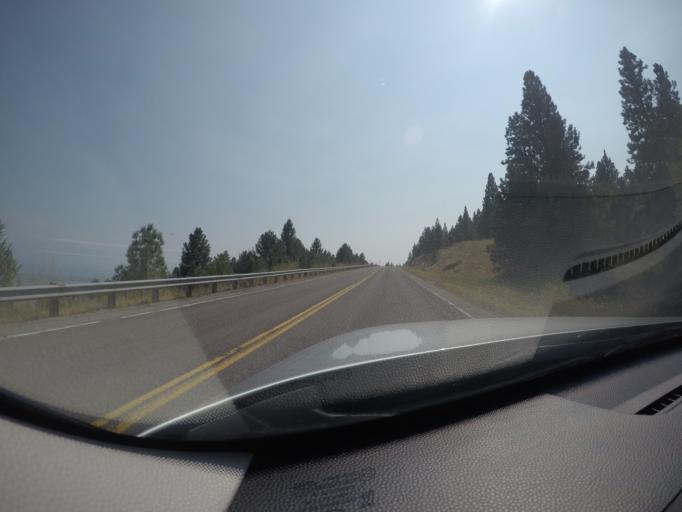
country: US
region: Montana
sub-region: Lake County
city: Polson
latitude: 47.7545
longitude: -114.1684
